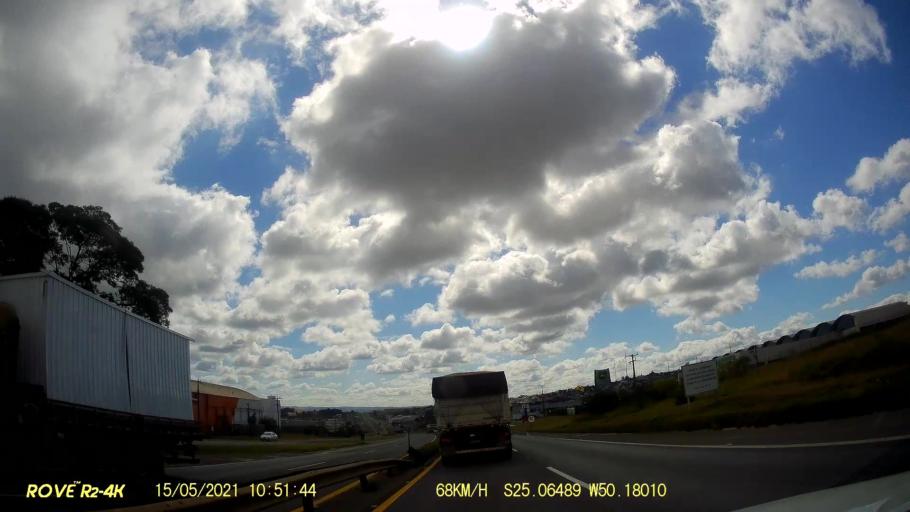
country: BR
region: Parana
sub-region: Ponta Grossa
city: Ponta Grossa
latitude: -25.0650
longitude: -50.1801
